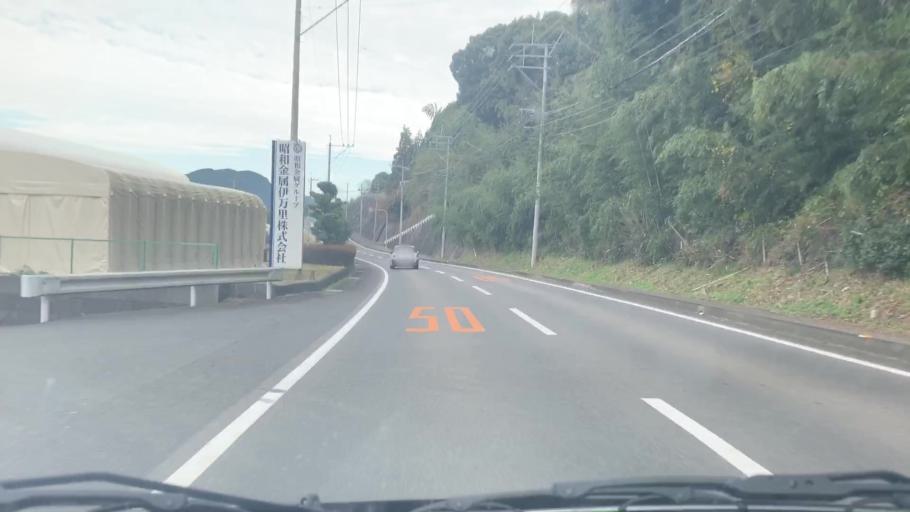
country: JP
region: Saga Prefecture
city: Imaricho-ko
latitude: 33.2885
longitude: 129.9709
